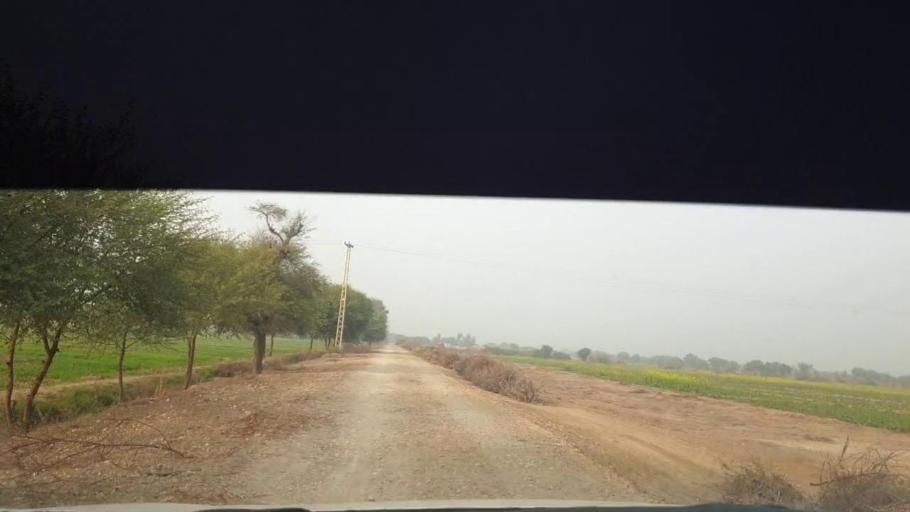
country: PK
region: Sindh
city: Berani
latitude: 25.8257
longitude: 68.8915
